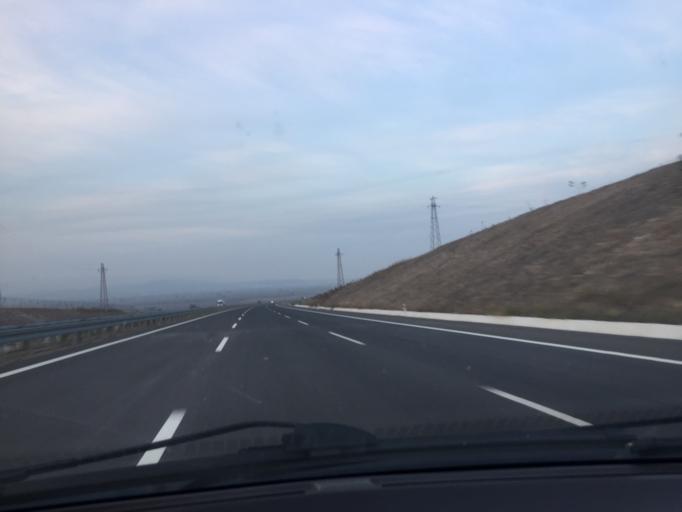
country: TR
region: Manisa
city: Halitpasa
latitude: 38.6958
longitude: 27.6423
